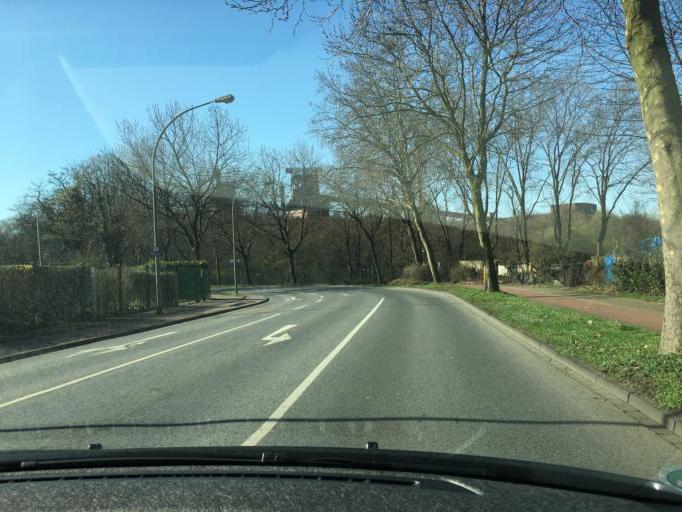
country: DE
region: North Rhine-Westphalia
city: Meiderich
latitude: 51.5117
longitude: 6.7437
